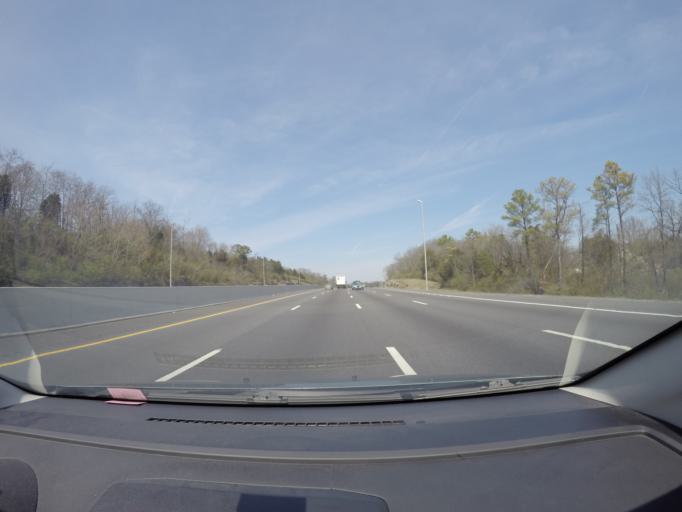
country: US
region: Tennessee
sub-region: Davidson County
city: Oak Hill
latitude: 36.1046
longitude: -86.7162
